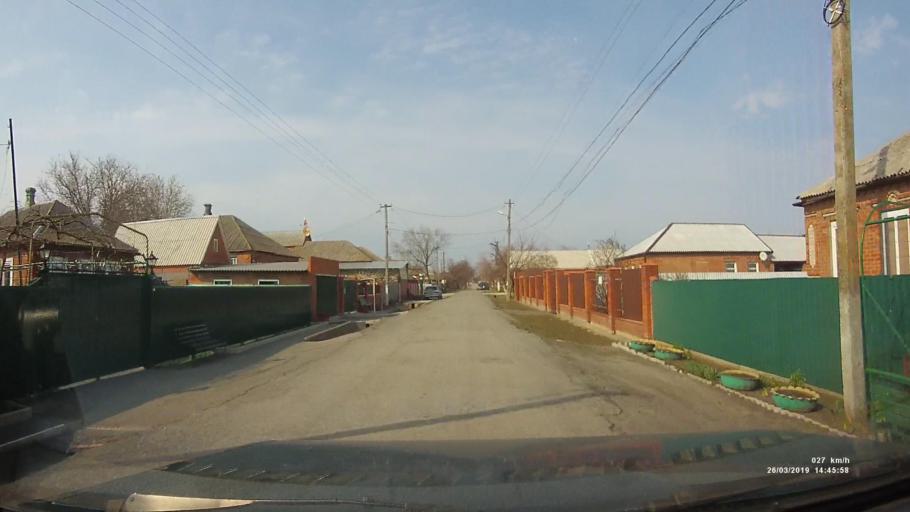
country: RU
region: Rostov
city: Novobessergenovka
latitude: 47.1845
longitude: 38.8610
